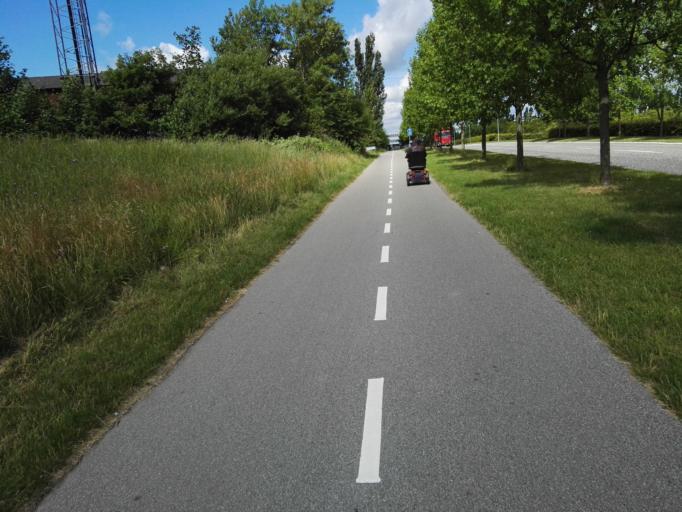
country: DK
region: Capital Region
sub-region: Ballerup Kommune
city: Ballerup
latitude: 55.7307
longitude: 12.3956
